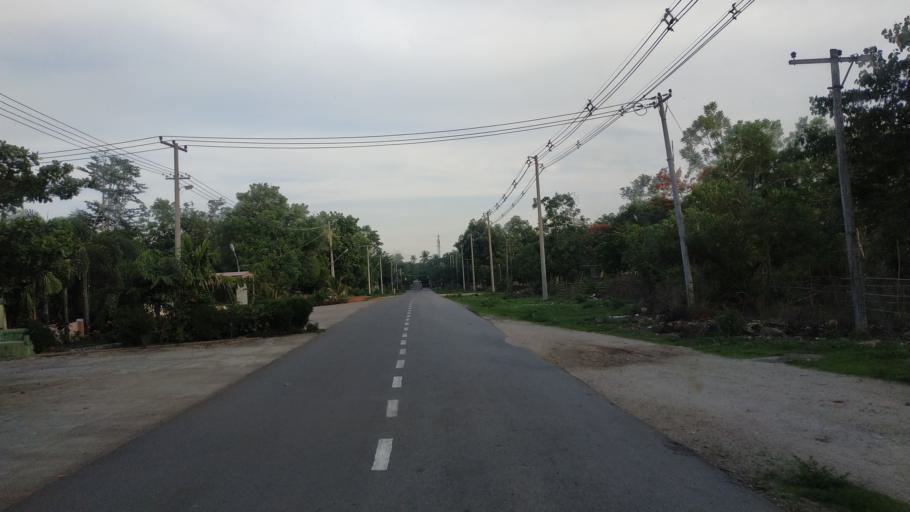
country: MM
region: Mon
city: Kyaikto
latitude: 17.4078
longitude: 97.0733
